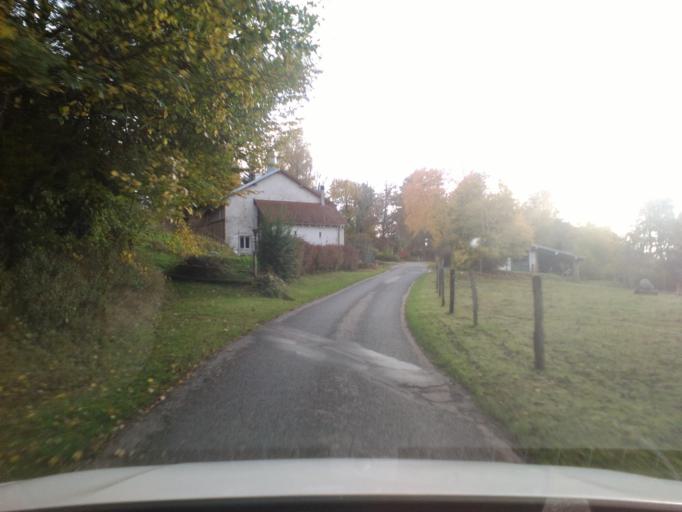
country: FR
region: Lorraine
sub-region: Departement des Vosges
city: Senones
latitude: 48.3416
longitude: 7.0159
